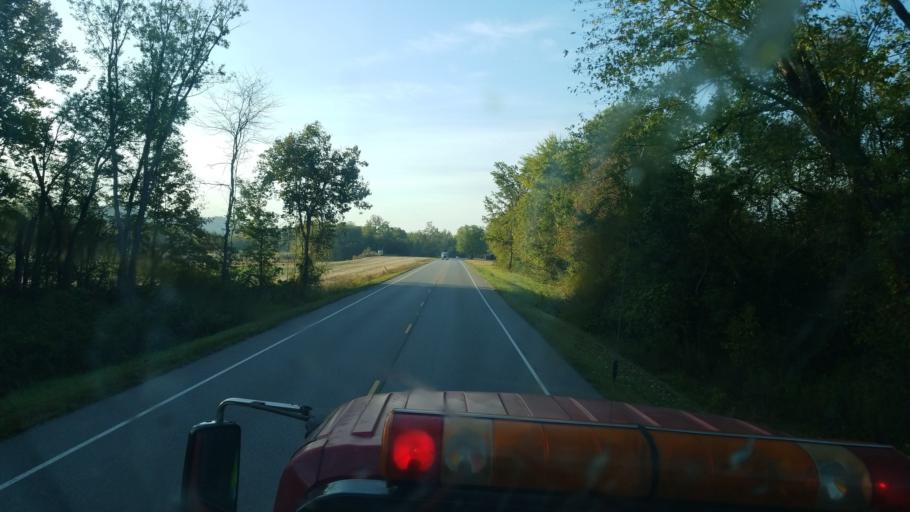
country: US
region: West Virginia
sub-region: Mason County
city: Point Pleasant
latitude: 38.8718
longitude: -82.1427
